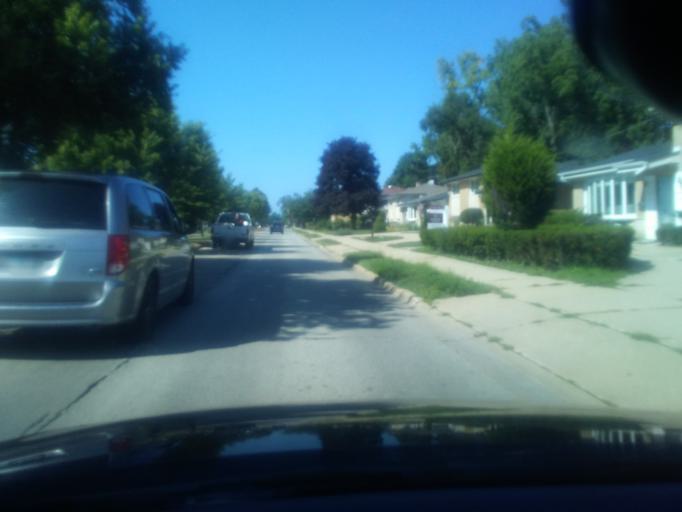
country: US
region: Illinois
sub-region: Cook County
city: Skokie
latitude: 42.0454
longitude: -87.7275
